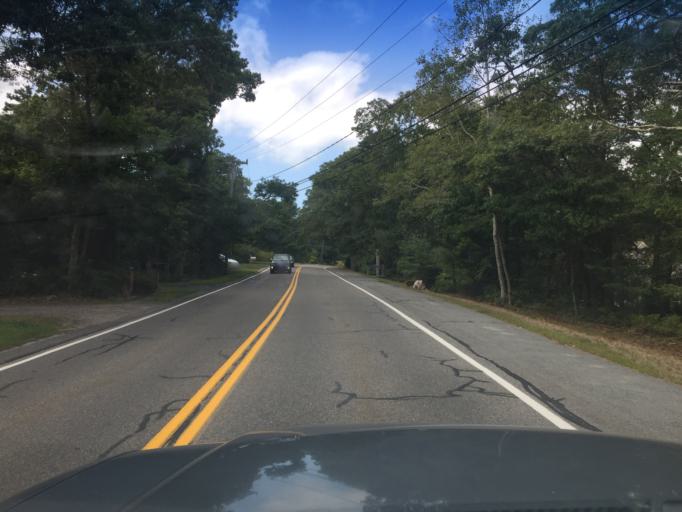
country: US
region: Massachusetts
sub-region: Barnstable County
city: Monument Beach
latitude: 41.7165
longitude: -70.5999
